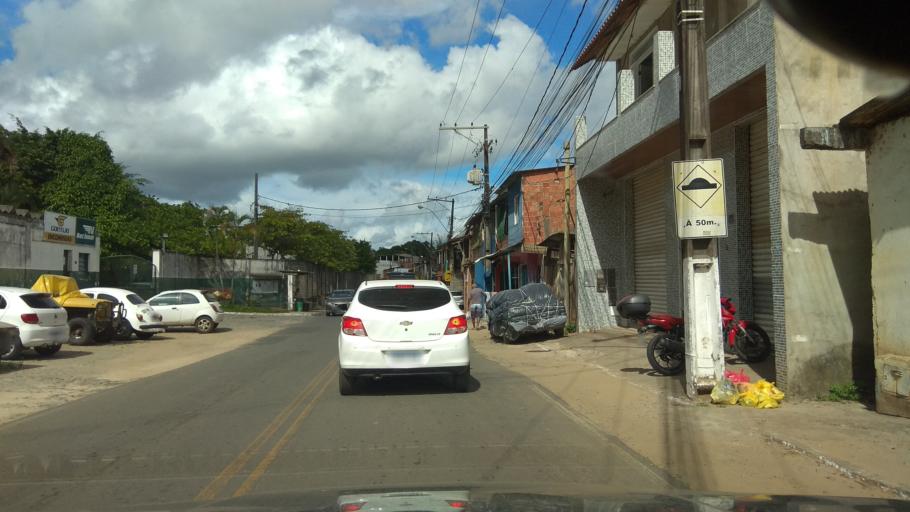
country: BR
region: Bahia
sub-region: Ilheus
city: Ilheus
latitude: -14.7922
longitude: -39.0628
